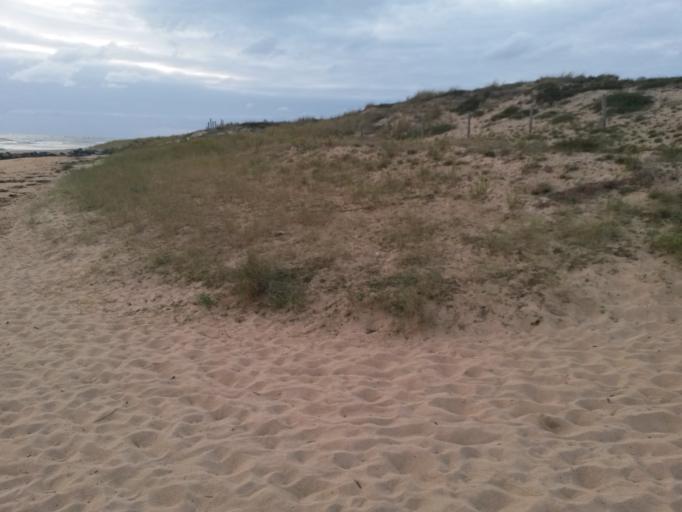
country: FR
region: Poitou-Charentes
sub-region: Departement de la Charente-Maritime
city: Dolus-d'Oleron
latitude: 45.9336
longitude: -1.3603
